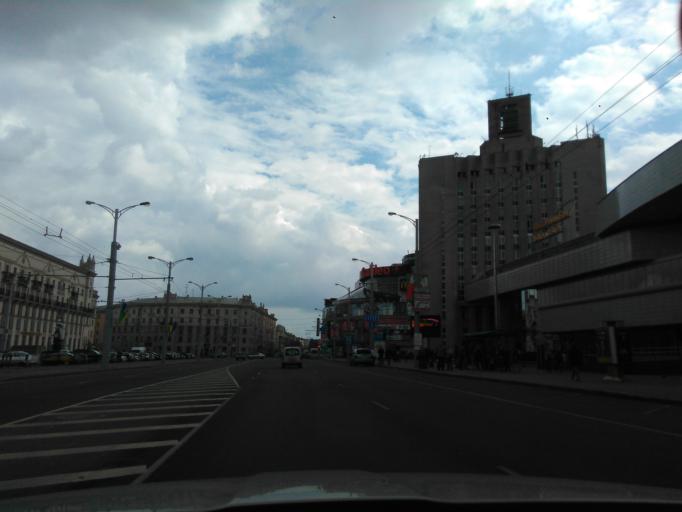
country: BY
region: Minsk
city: Minsk
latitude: 53.8914
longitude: 27.5508
